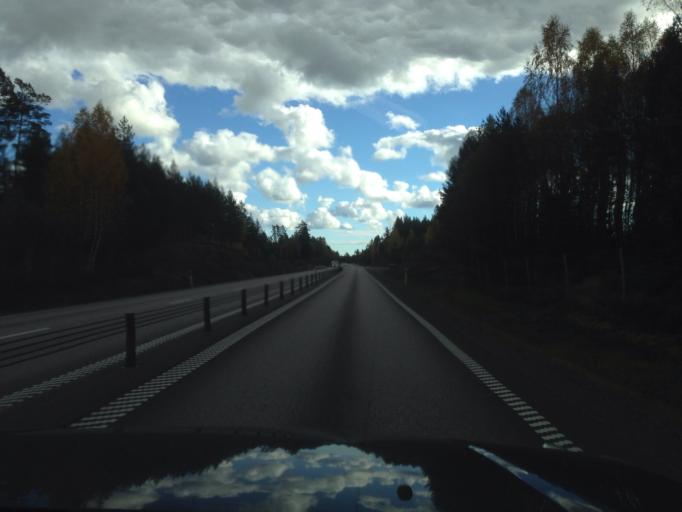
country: SE
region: Dalarna
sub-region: Hedemora Kommun
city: Langshyttan
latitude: 60.5512
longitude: 16.1198
